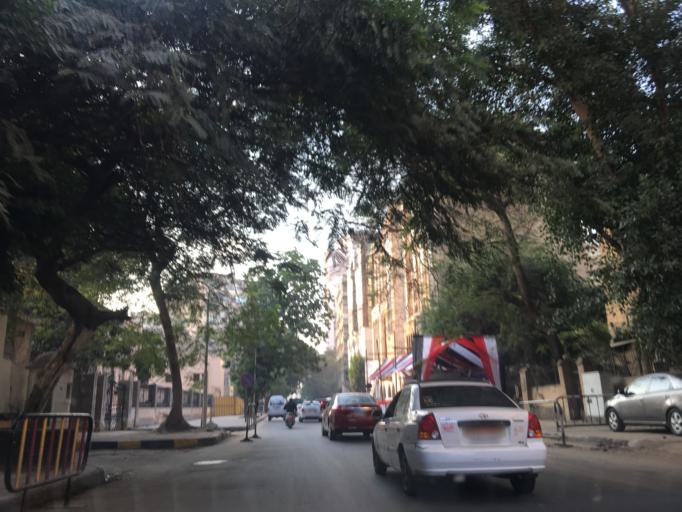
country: EG
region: Muhafazat al Qahirah
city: Cairo
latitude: 30.0417
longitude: 31.2353
